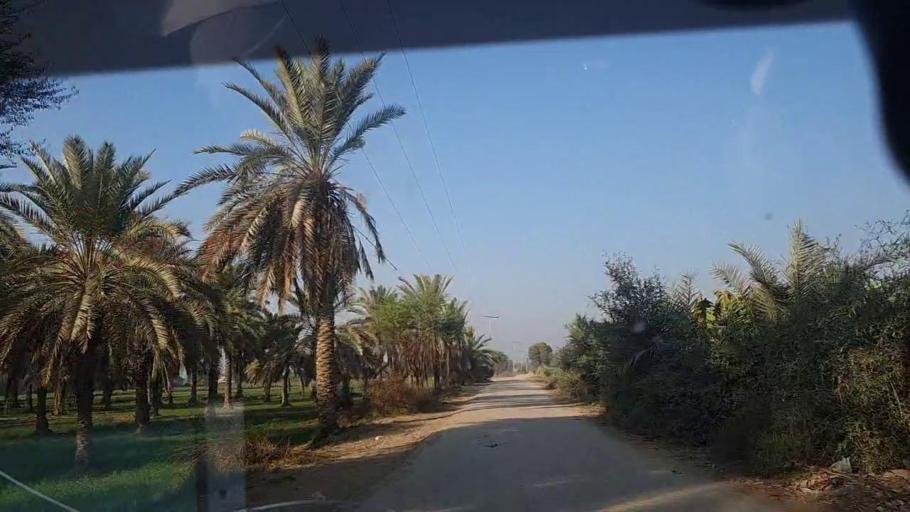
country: PK
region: Sindh
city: Sobhadero
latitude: 27.2481
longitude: 68.3497
